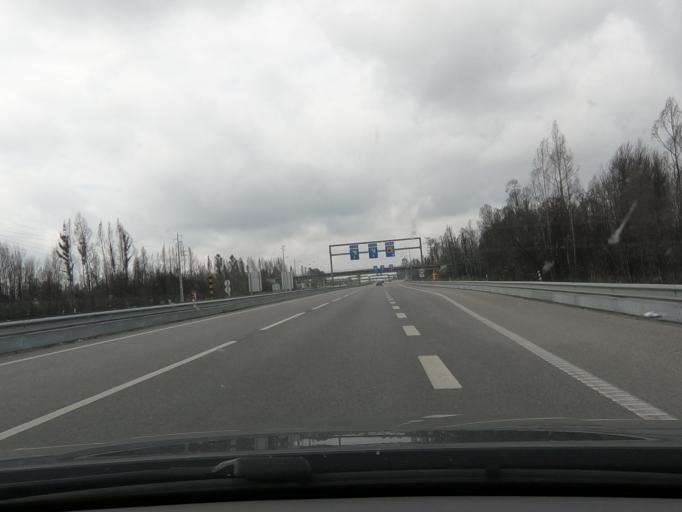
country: PT
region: Coimbra
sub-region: Mira
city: Mira
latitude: 40.4485
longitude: -8.7010
